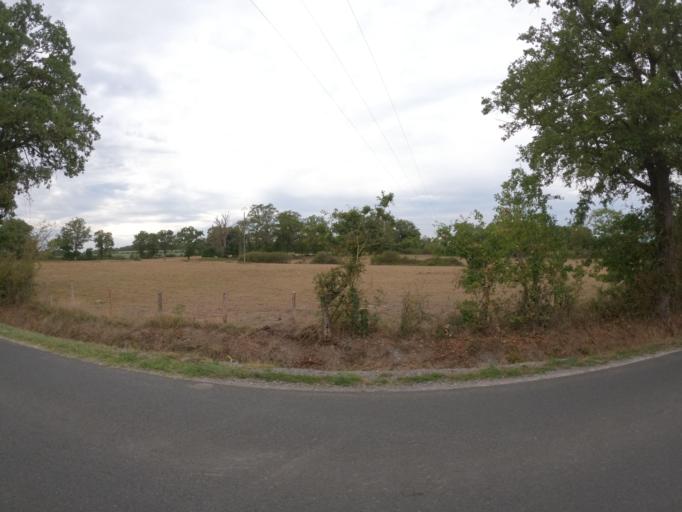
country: FR
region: Poitou-Charentes
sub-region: Departement de la Vienne
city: Saulge
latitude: 46.4022
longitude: 0.8556
